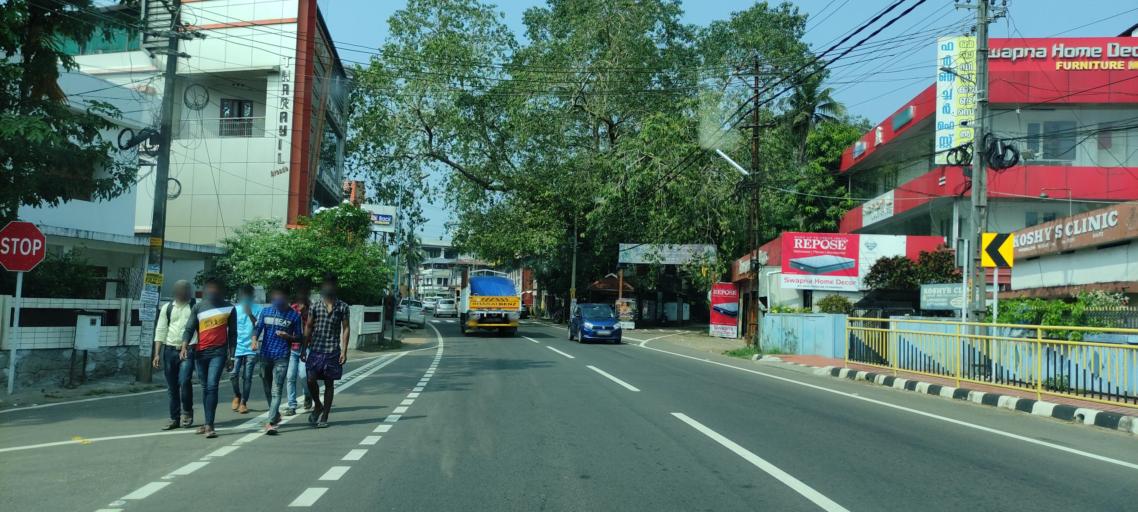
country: IN
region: Kerala
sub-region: Pattanamtitta
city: Adur
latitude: 9.2286
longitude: 76.6778
